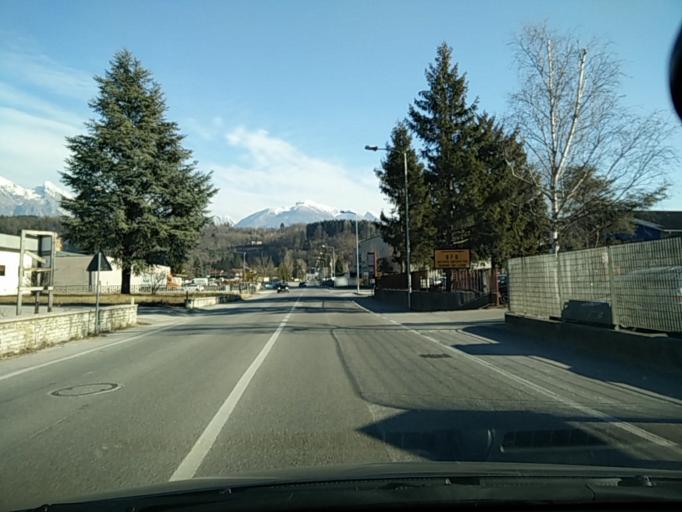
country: IT
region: Veneto
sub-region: Provincia di Belluno
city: Soccher-Paiane-Casan-Arsie
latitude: 46.1511
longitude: 12.3228
